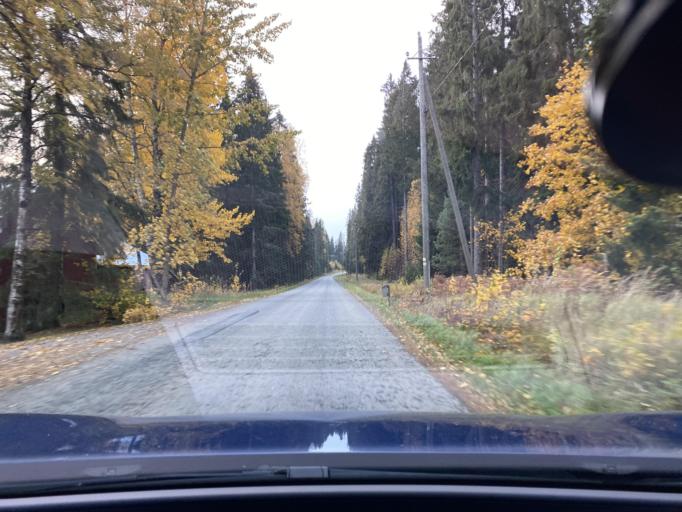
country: FI
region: Varsinais-Suomi
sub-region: Loimaa
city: Alastaro
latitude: 61.0808
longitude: 22.9478
